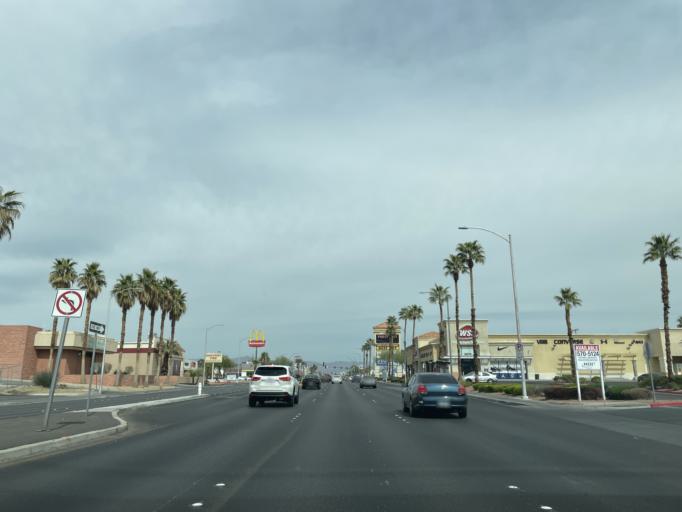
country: US
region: Nevada
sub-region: Clark County
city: Winchester
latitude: 36.1179
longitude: -115.1376
